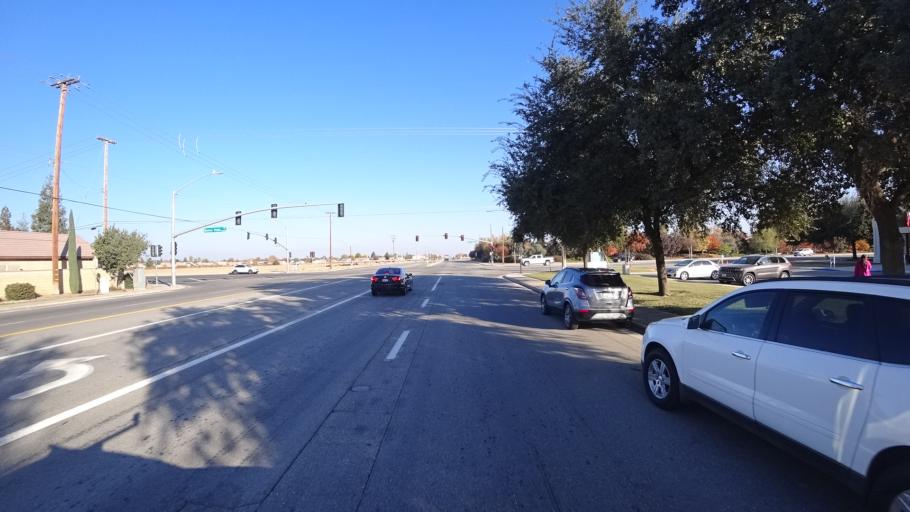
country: US
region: California
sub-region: Kern County
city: Rosedale
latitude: 35.2962
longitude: -119.1288
